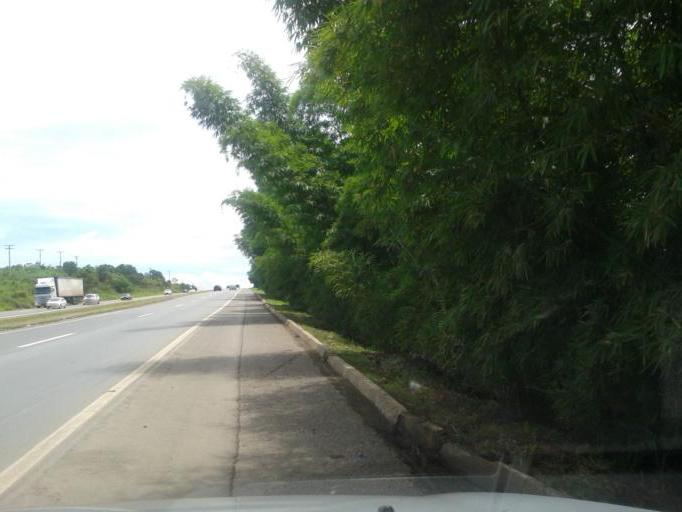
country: BR
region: Goias
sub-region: Aparecida De Goiania
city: Aparecida de Goiania
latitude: -16.8698
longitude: -49.2508
